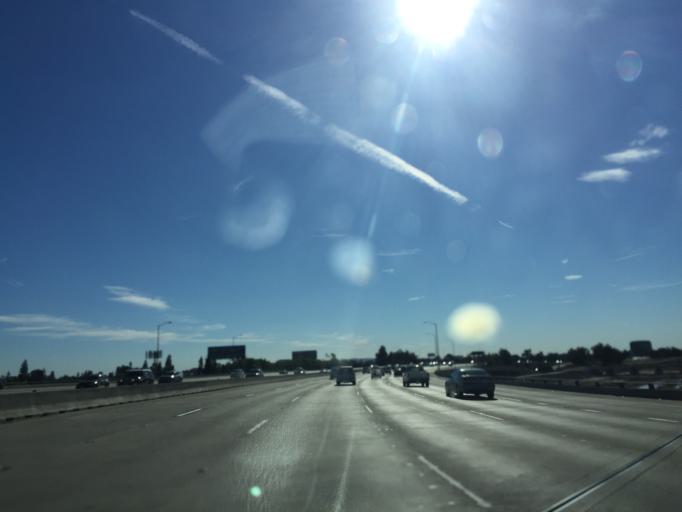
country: US
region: California
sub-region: Orange County
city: Orange
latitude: 33.8004
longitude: -117.8783
